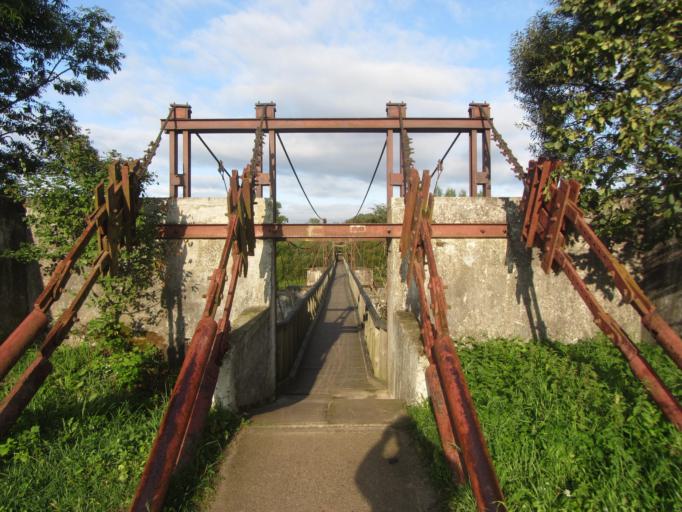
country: LT
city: Priekule
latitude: 55.4874
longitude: 21.3640
